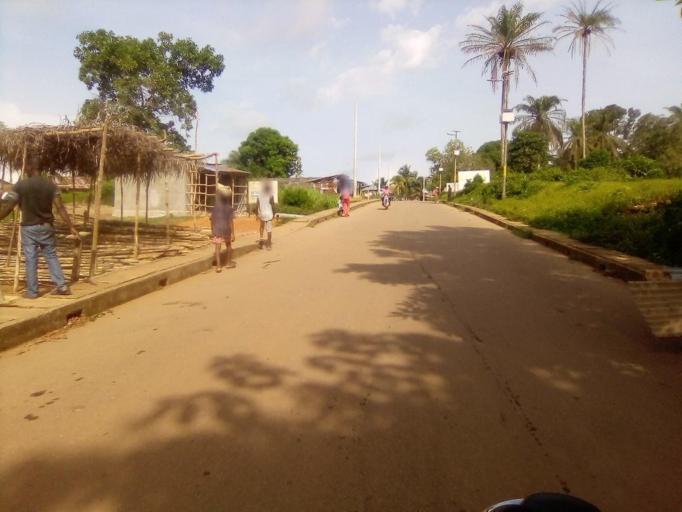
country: SL
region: Southern Province
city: Pujehun
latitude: 7.3598
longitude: -11.7274
